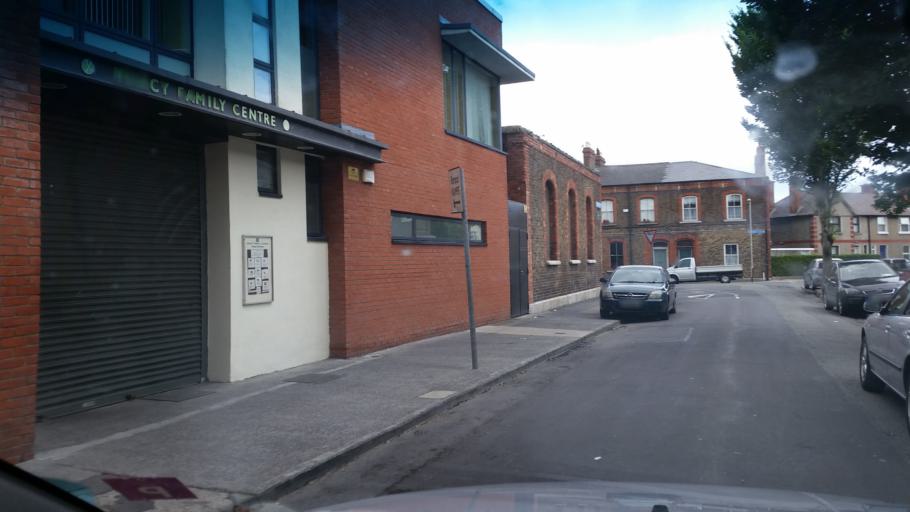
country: IE
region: Leinster
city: Rialto
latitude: 53.3369
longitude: -6.2817
